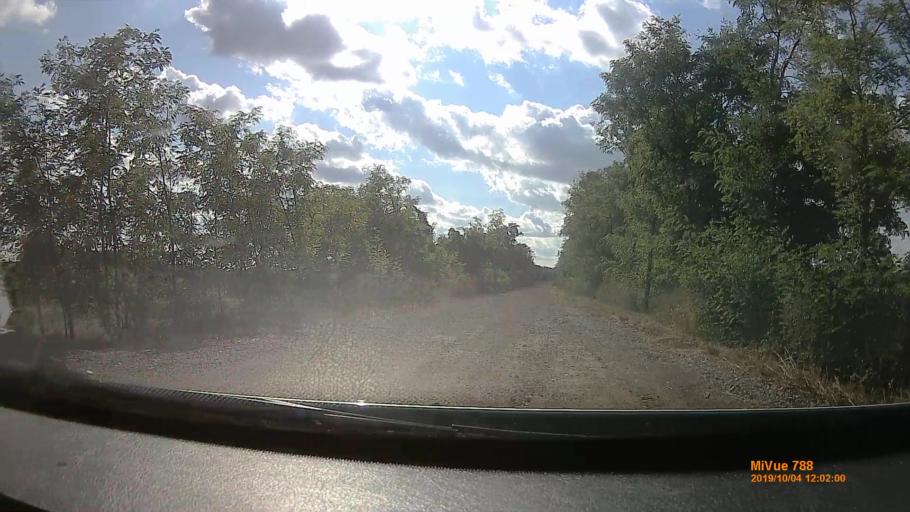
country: HU
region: Szabolcs-Szatmar-Bereg
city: Nyirtelek
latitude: 48.0199
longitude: 21.6781
